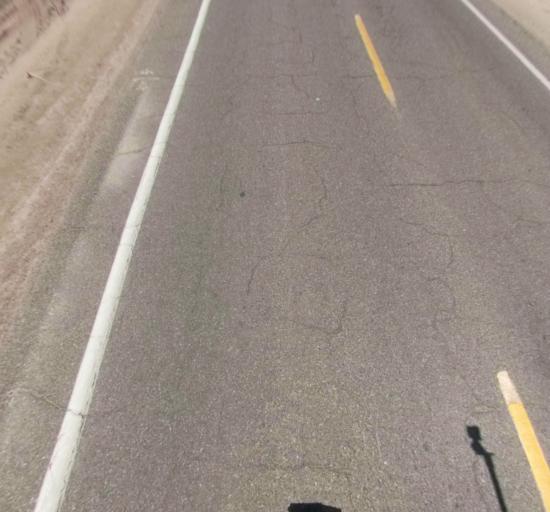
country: US
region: California
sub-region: Madera County
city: Fairmead
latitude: 36.9585
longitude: -120.2021
